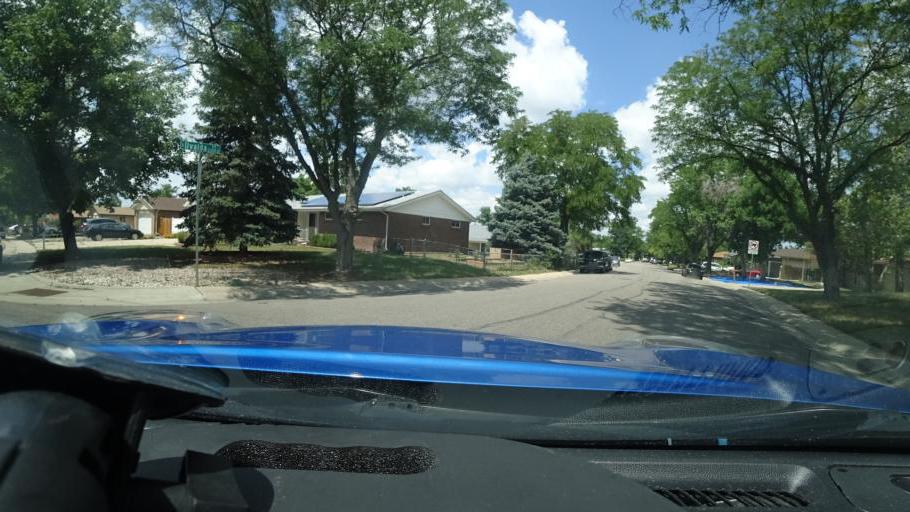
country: US
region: Colorado
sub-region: Adams County
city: Aurora
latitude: 39.7051
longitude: -104.8369
